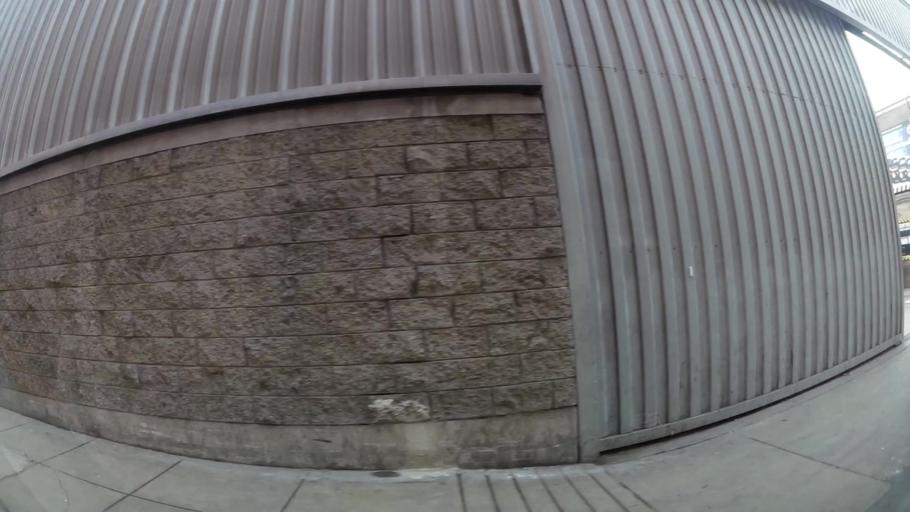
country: PE
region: Lima
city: Lima
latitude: -12.0471
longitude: -77.0386
